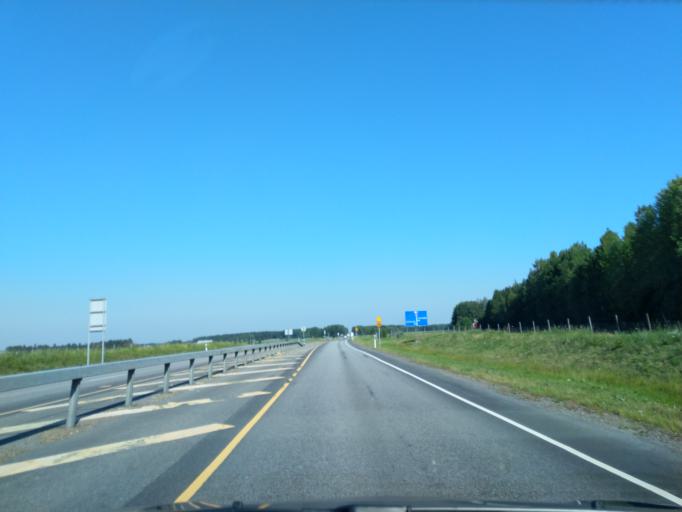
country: FI
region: Varsinais-Suomi
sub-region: Loimaa
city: Alastaro
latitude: 61.0595
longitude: 22.9423
